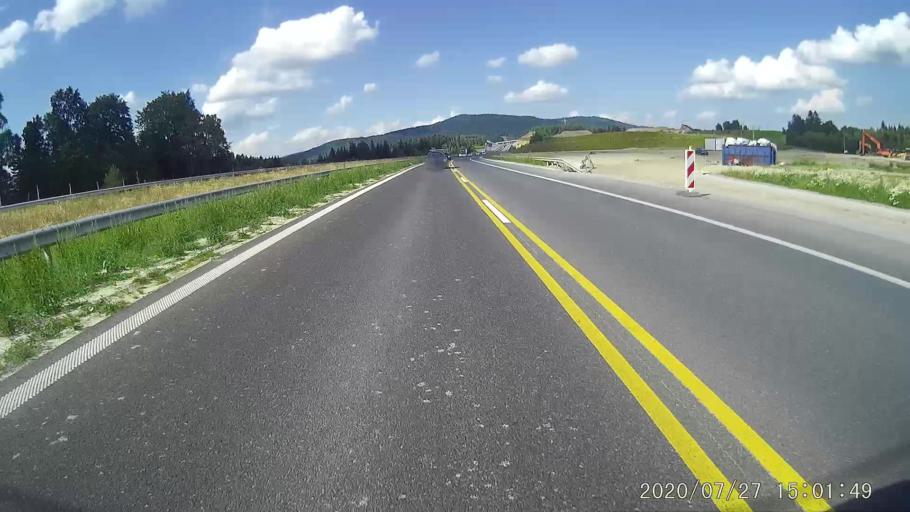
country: PL
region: Lesser Poland Voivodeship
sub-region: Powiat suski
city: Letownia
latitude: 49.6782
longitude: 19.8887
